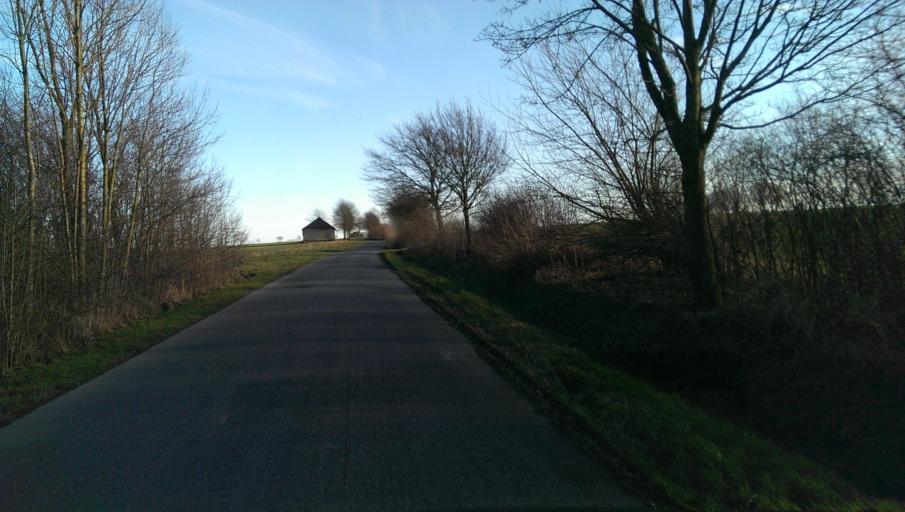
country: DE
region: North Rhine-Westphalia
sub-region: Regierungsbezirk Arnsberg
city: Ruthen
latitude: 51.5217
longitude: 8.4171
